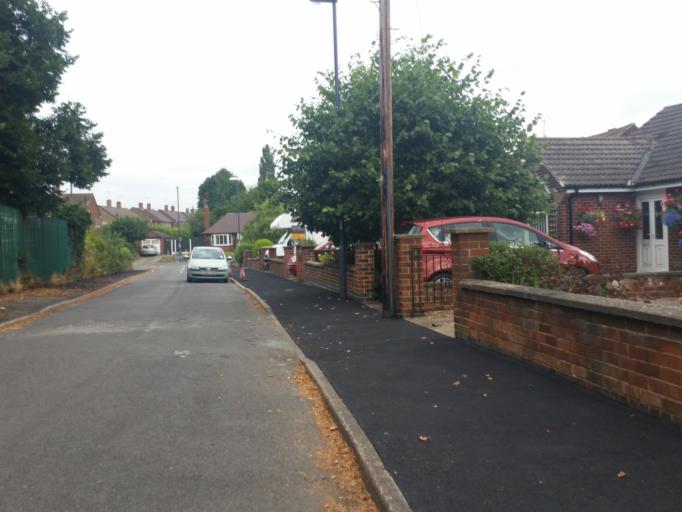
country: GB
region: England
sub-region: Derbyshire
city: Borrowash
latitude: 52.8938
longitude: -1.4192
